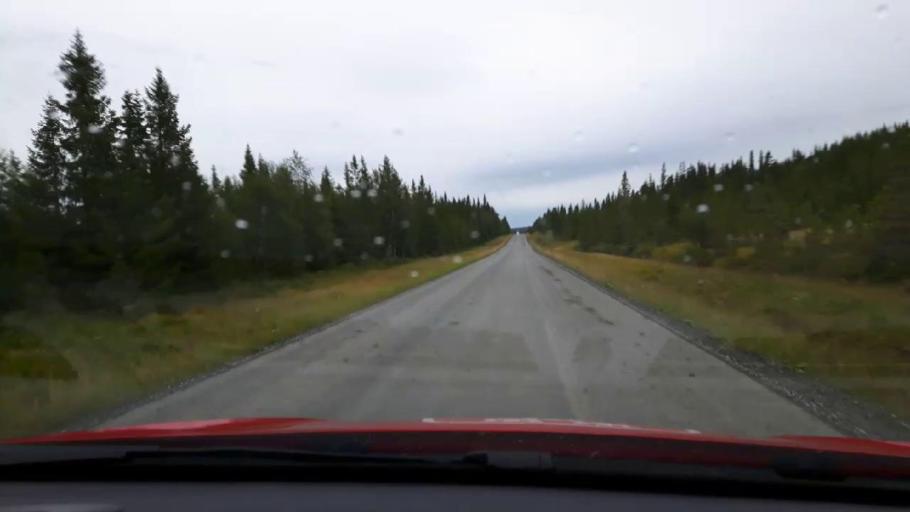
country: SE
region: Jaemtland
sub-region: Are Kommun
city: Are
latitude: 63.4455
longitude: 13.2329
